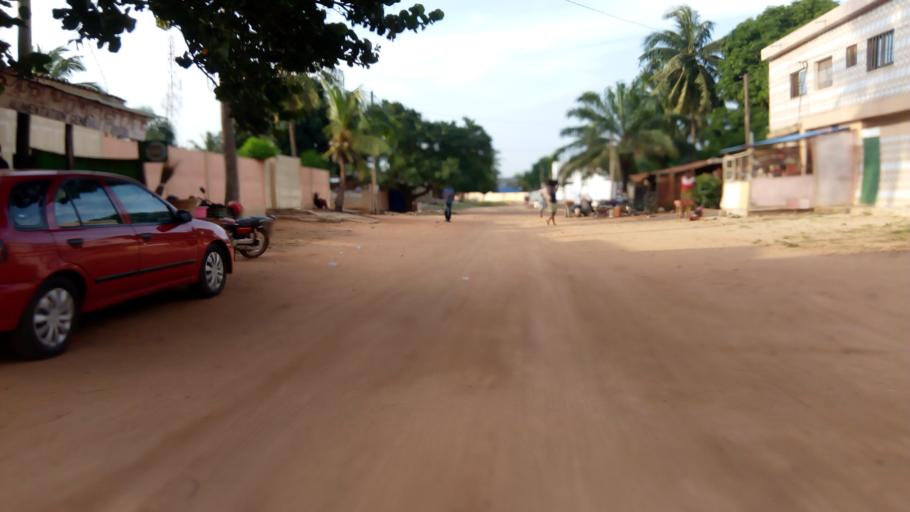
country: TG
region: Maritime
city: Lome
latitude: 6.1846
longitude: 1.1824
